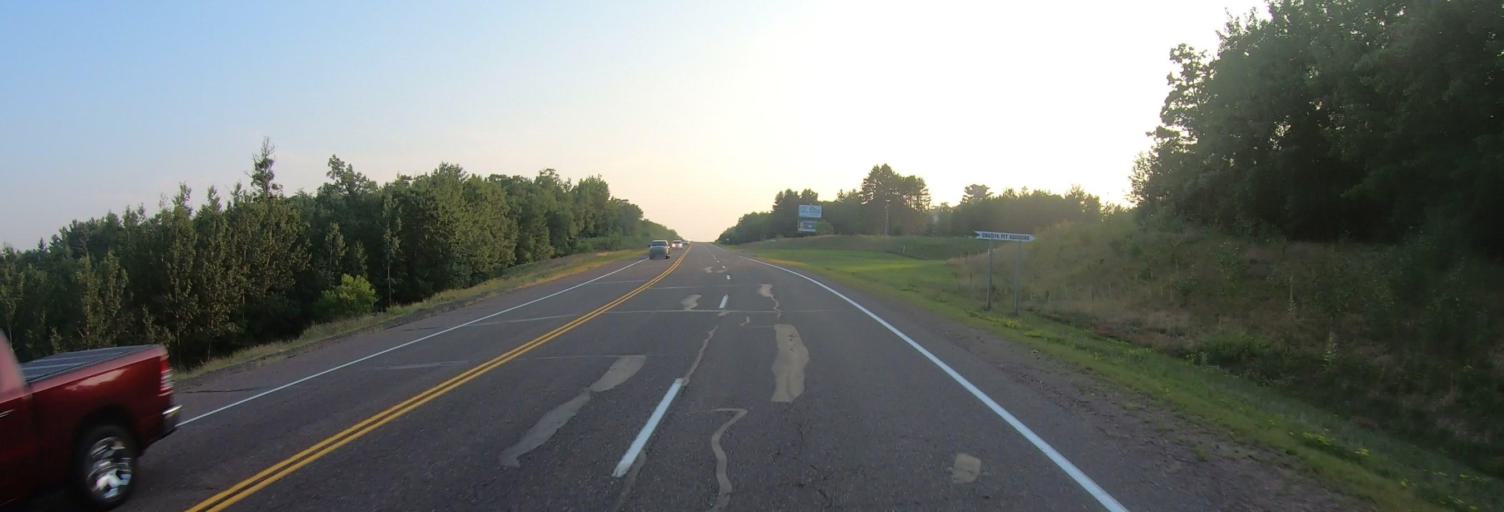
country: US
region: Wisconsin
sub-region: Burnett County
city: Siren
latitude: 45.7841
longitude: -92.4220
